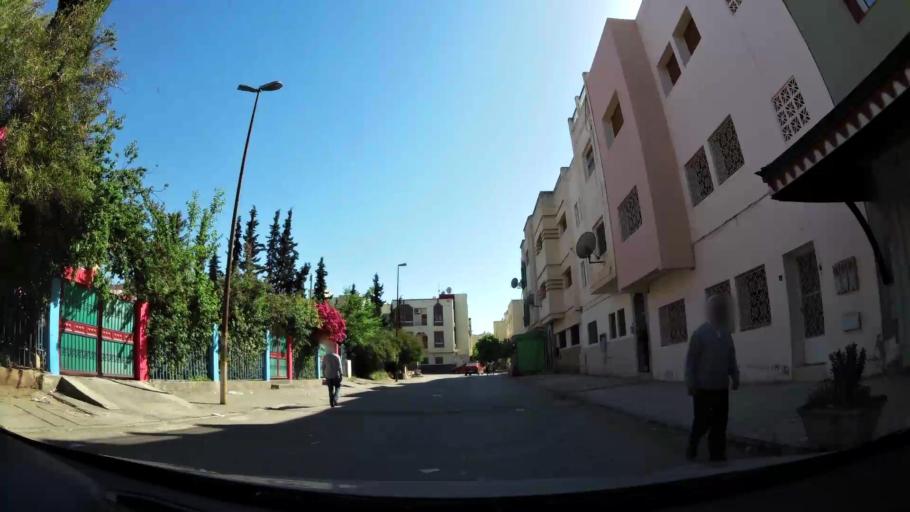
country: MA
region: Fes-Boulemane
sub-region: Fes
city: Fes
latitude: 34.0193
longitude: -4.9758
